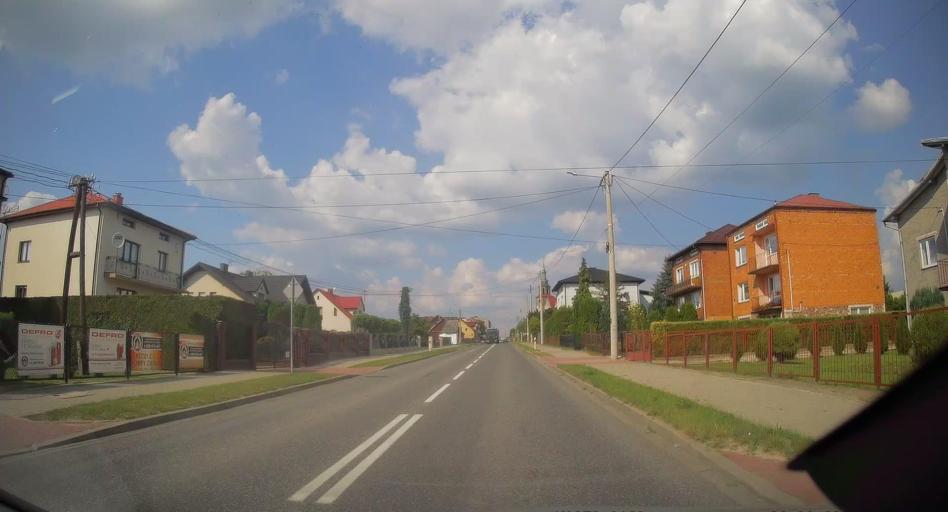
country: PL
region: Swietokrzyskie
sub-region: Powiat kielecki
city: Lopuszno
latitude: 50.9453
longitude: 20.2483
